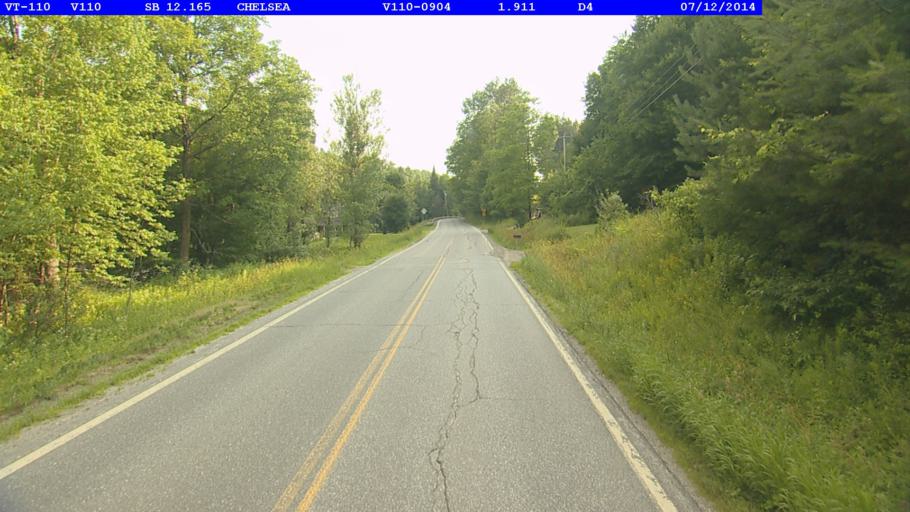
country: US
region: Vermont
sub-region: Orange County
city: Chelsea
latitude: 43.9745
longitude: -72.4510
